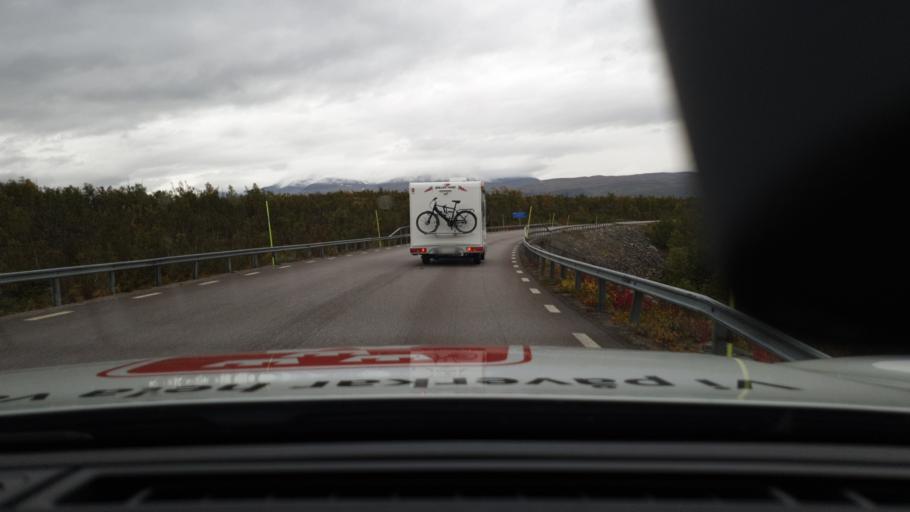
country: NO
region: Troms
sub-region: Bardu
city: Setermoen
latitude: 68.4408
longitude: 18.5884
